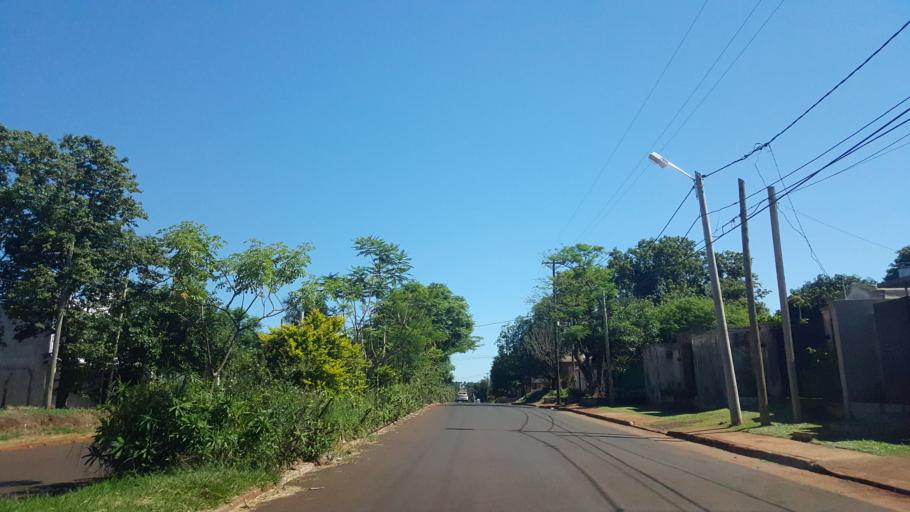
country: AR
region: Misiones
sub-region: Departamento de Capital
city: Posadas
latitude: -27.3866
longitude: -55.9307
